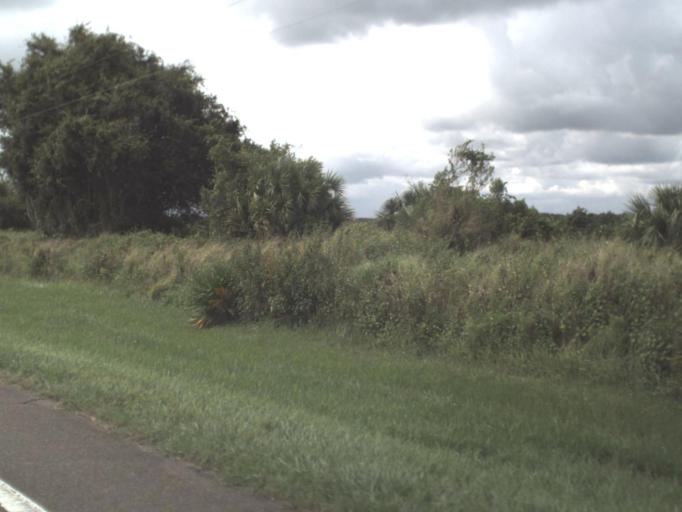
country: US
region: Florida
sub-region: Sarasota County
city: North Port
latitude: 27.1933
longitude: -82.1280
